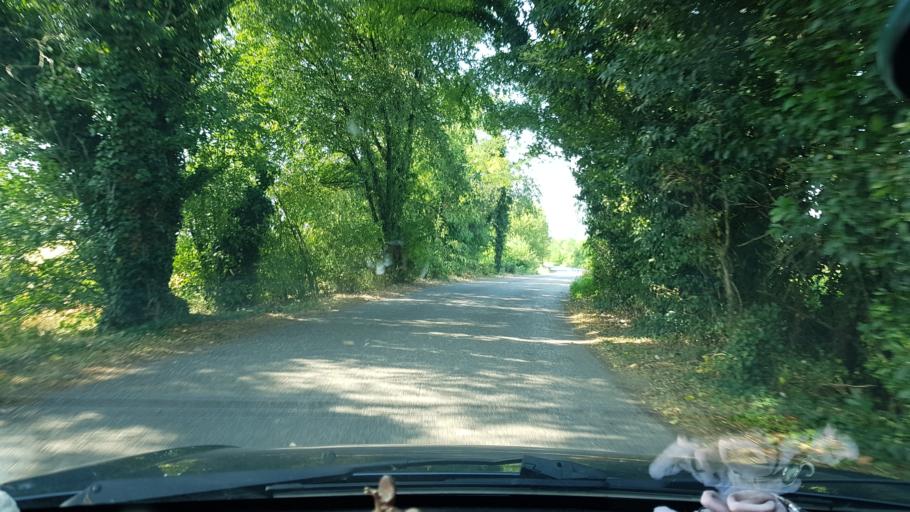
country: IT
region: Friuli Venezia Giulia
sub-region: Provincia di Gorizia
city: Fogliano
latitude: 45.8631
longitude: 13.4792
